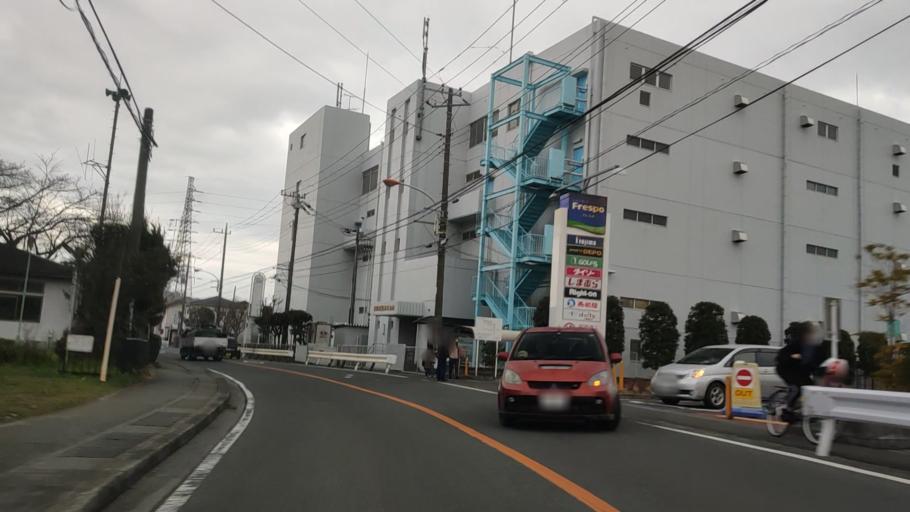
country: JP
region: Kanagawa
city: Odawara
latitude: 35.2836
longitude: 139.1940
